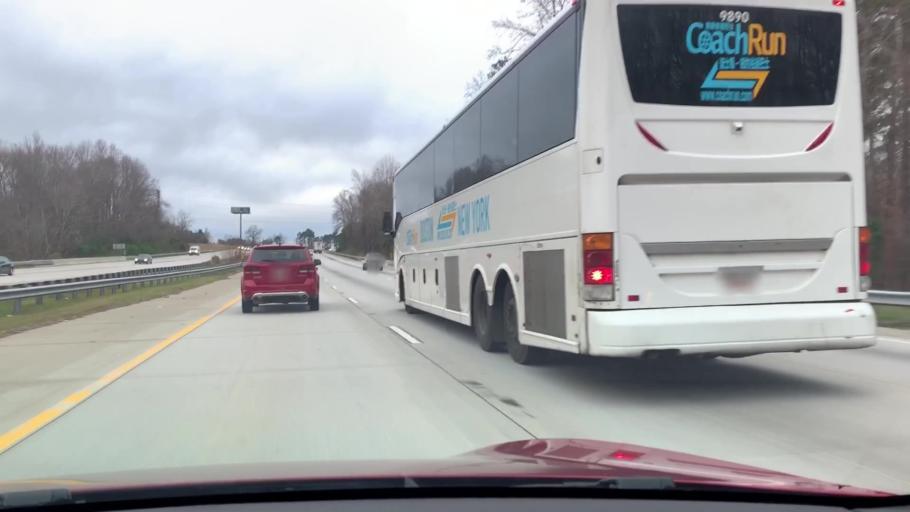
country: US
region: South Carolina
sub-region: Florence County
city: Florence
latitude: 34.2485
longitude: -79.7658
